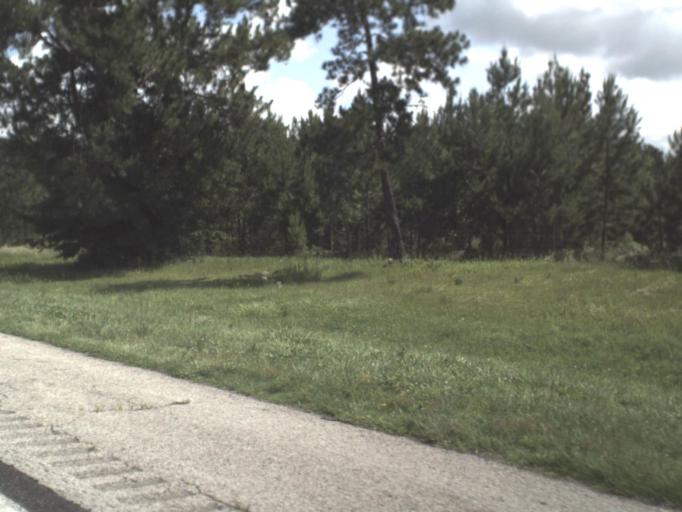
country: US
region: Florida
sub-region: Alachua County
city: Alachua
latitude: 29.7827
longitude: -82.5126
